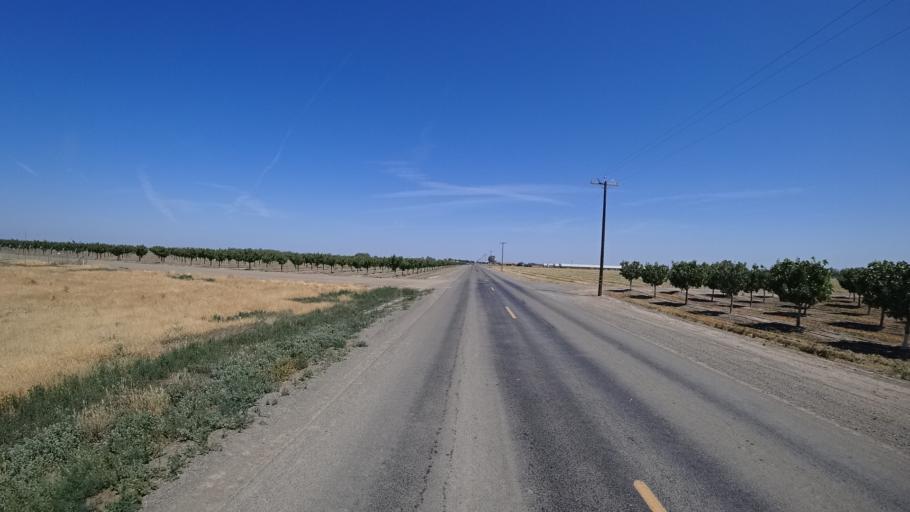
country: US
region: California
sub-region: Kings County
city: Stratford
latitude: 36.2292
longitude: -119.7983
